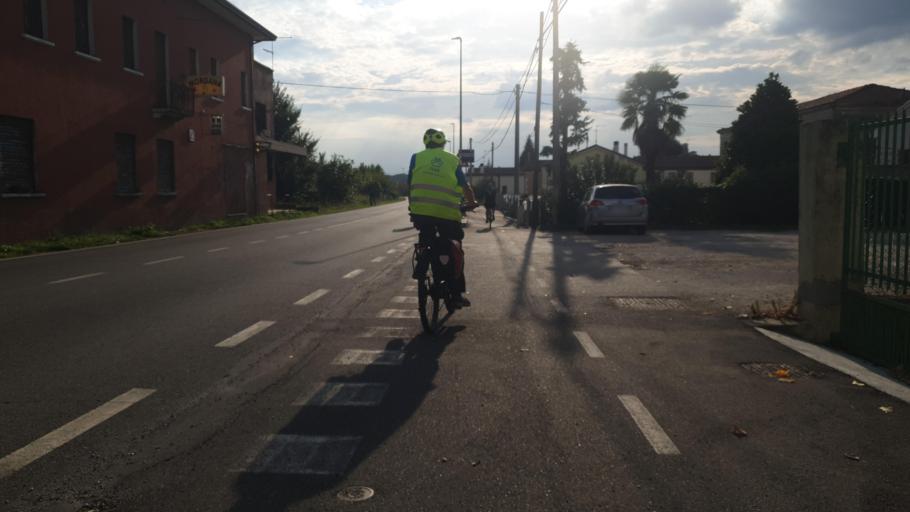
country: IT
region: Veneto
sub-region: Provincia di Padova
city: Montagnana
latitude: 45.2507
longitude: 11.4797
